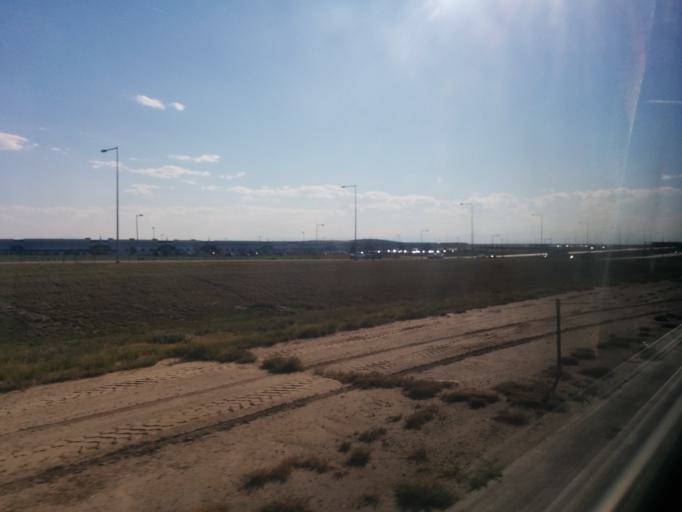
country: US
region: Colorado
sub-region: Adams County
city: Aurora
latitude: 39.8342
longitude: -104.6957
